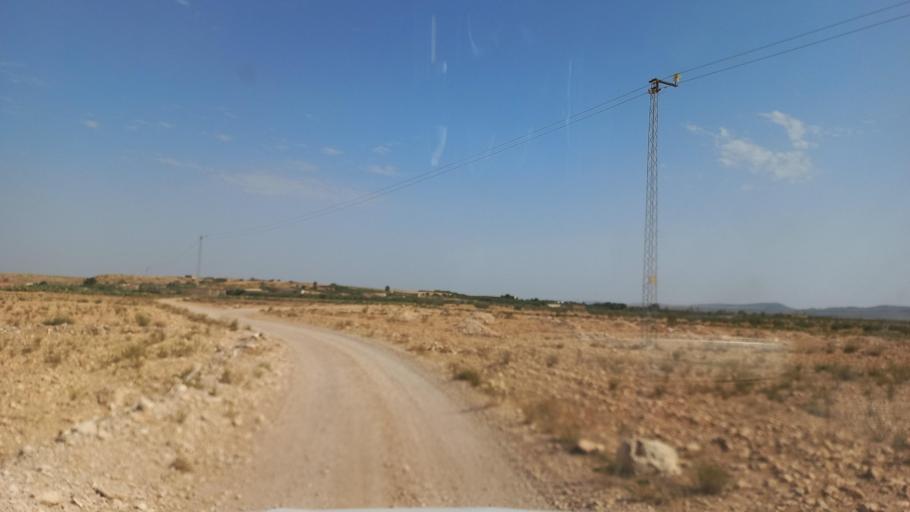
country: TN
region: Al Qasrayn
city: Kasserine
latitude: 35.2791
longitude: 8.9630
